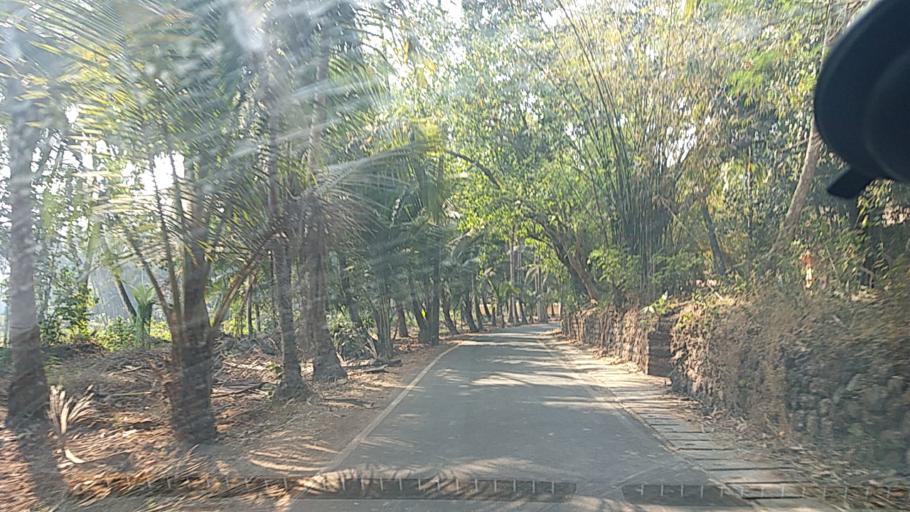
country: IN
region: Goa
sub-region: South Goa
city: Sancoale
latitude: 15.3612
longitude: 73.8876
